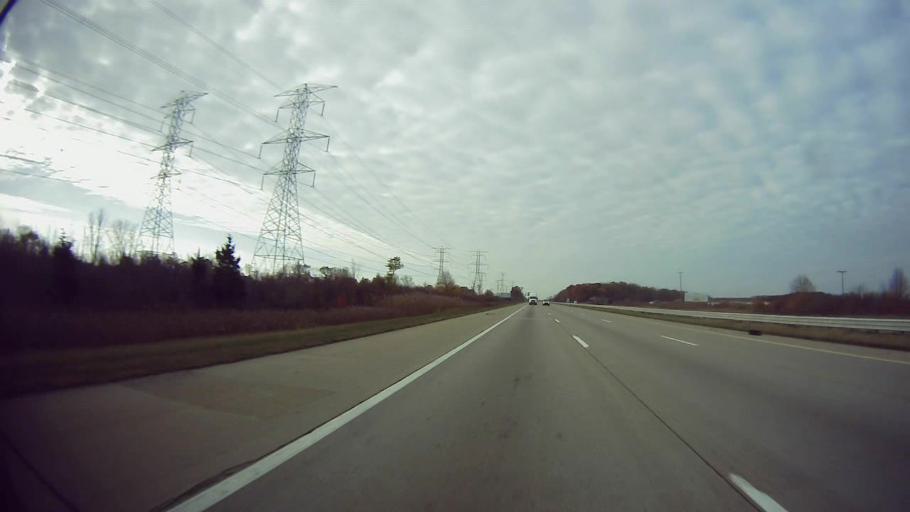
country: US
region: Michigan
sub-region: Monroe County
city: South Rockwood
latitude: 42.0520
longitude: -83.2695
